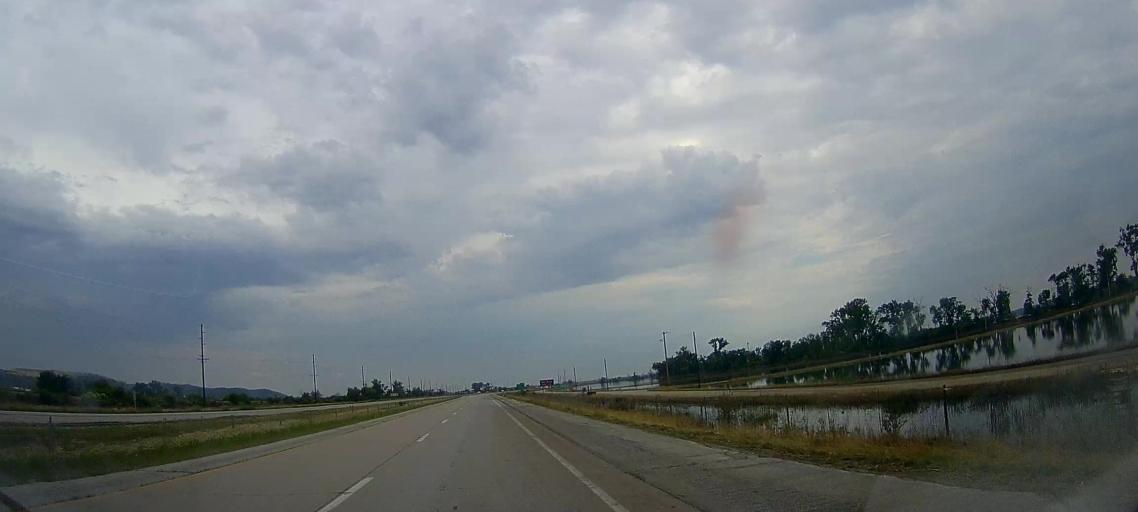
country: US
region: Iowa
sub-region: Pottawattamie County
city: Carter Lake
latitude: 41.3699
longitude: -95.8995
